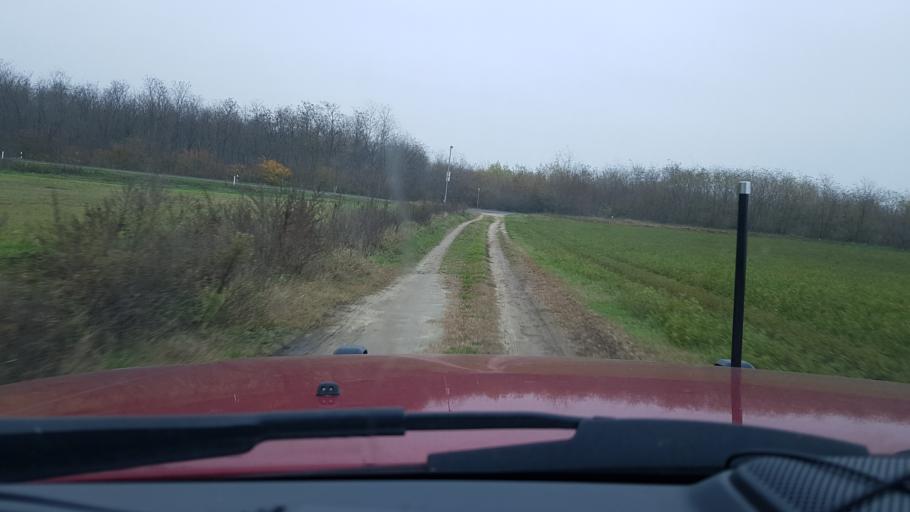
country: HU
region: Pest
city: Felsopakony
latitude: 47.3347
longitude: 19.2909
